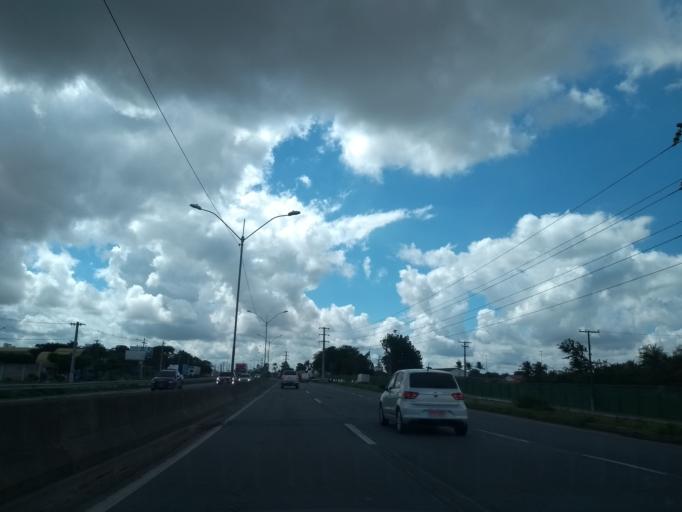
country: BR
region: Bahia
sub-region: Feira De Santana
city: Feira de Santana
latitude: -12.2804
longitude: -38.9429
